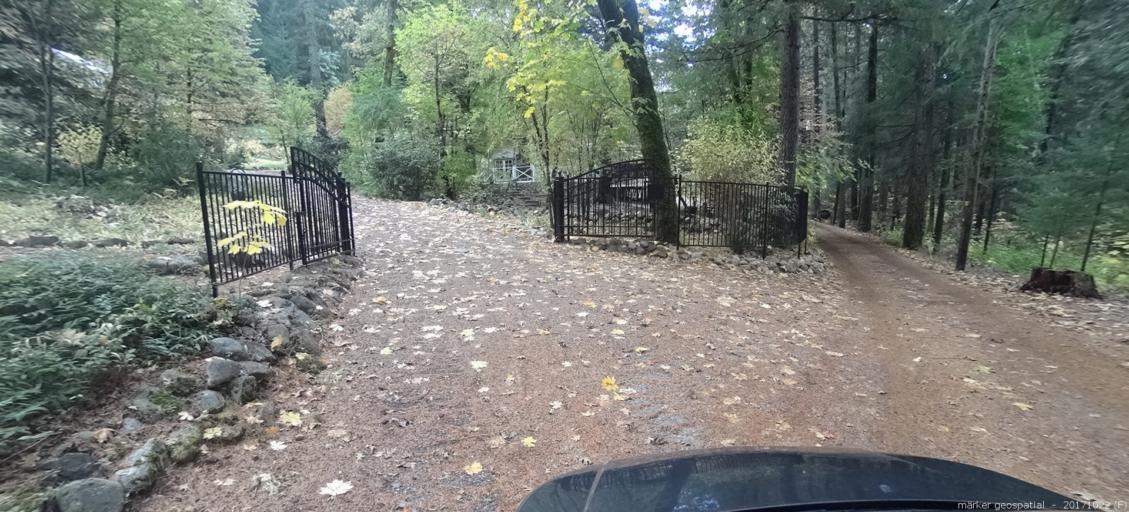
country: US
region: California
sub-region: Siskiyou County
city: Dunsmuir
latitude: 41.1289
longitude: -122.3195
